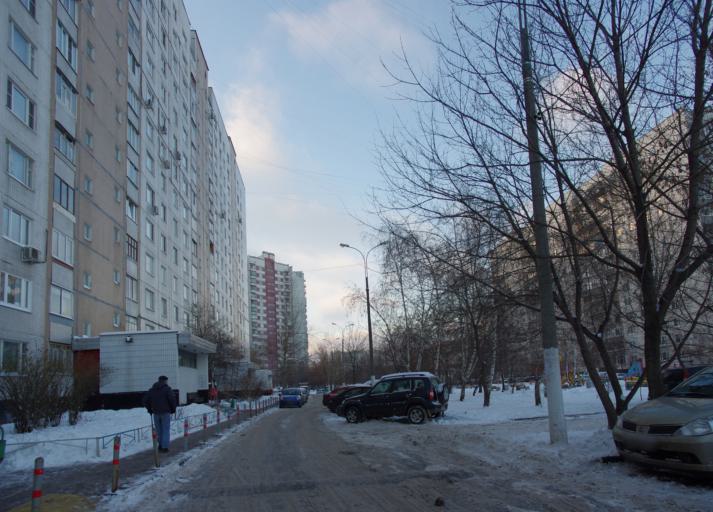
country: RU
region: Moscow
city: Orekhovo-Borisovo Severnoye
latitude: 55.6394
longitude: 37.6745
